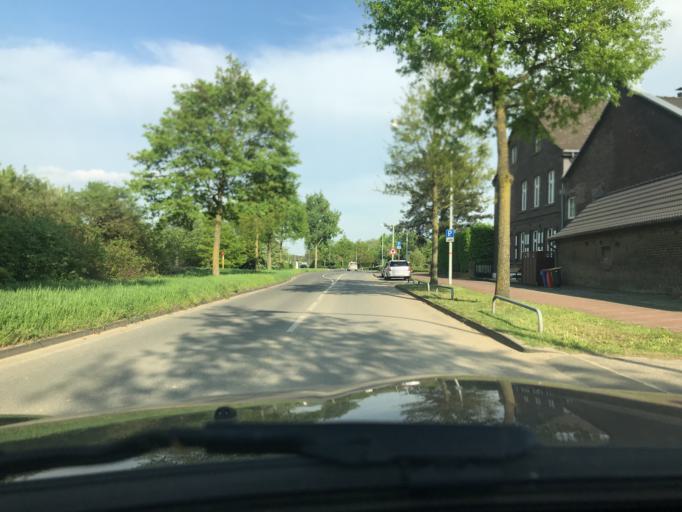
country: DE
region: North Rhine-Westphalia
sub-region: Regierungsbezirk Dusseldorf
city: Krefeld
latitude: 51.3034
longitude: 6.5641
